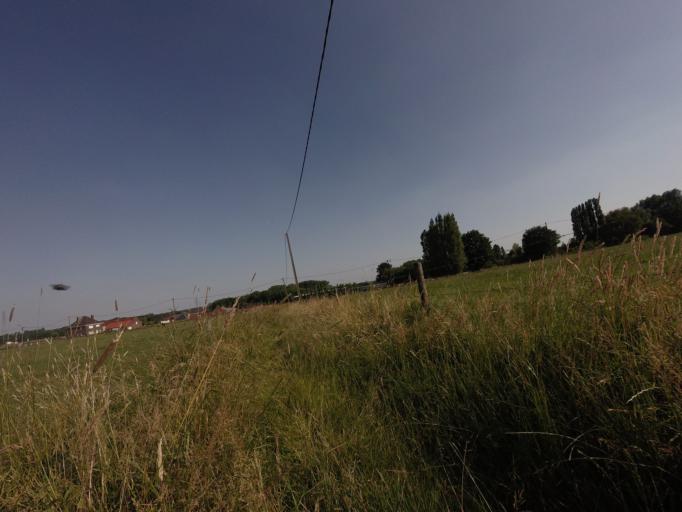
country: BE
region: Flanders
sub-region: Provincie Antwerpen
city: Rumst
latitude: 51.0945
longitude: 4.4561
